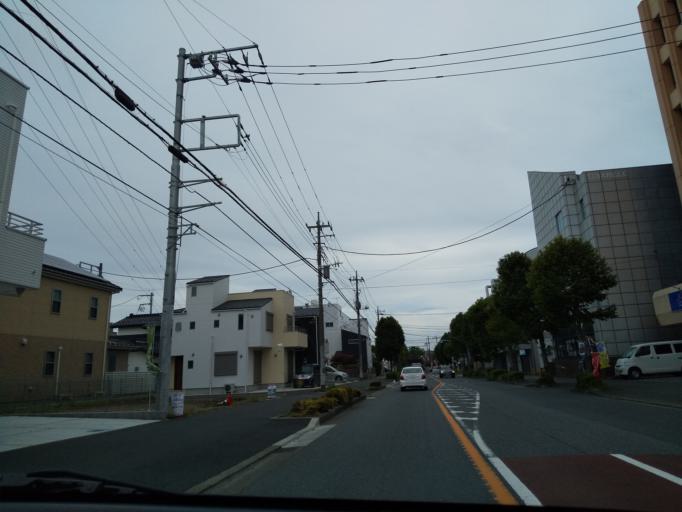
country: JP
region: Kanagawa
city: Zama
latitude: 35.5155
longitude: 139.4061
